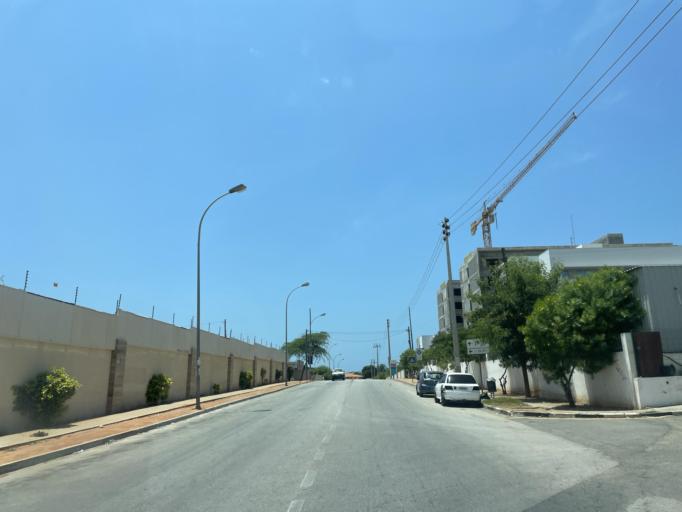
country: AO
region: Luanda
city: Luanda
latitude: -8.9266
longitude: 13.1855
